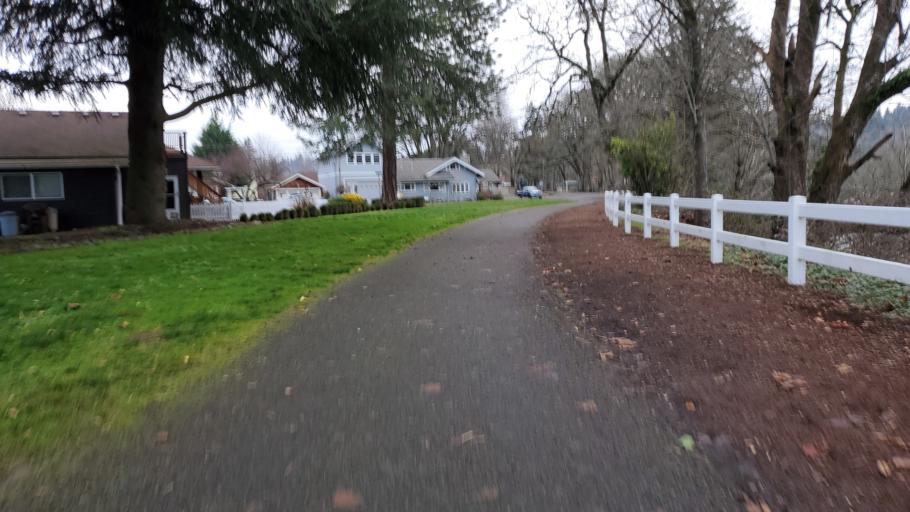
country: US
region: Oregon
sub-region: Clackamas County
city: Gladstone
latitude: 45.3790
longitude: -122.5907
